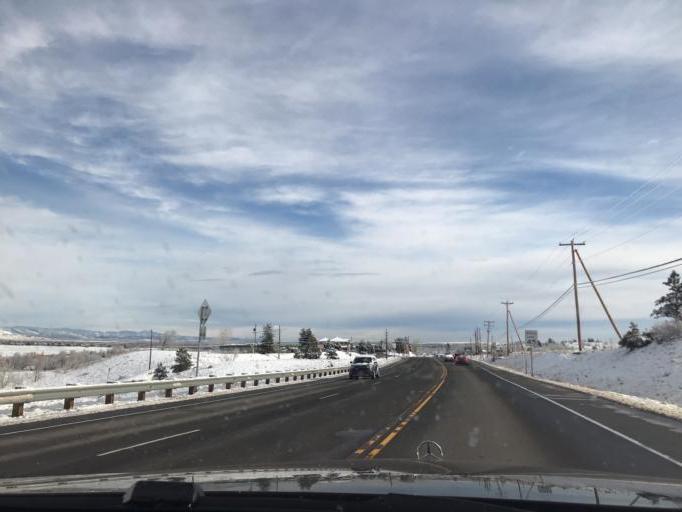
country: US
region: Colorado
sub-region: Boulder County
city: Superior
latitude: 39.9504
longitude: -105.2338
